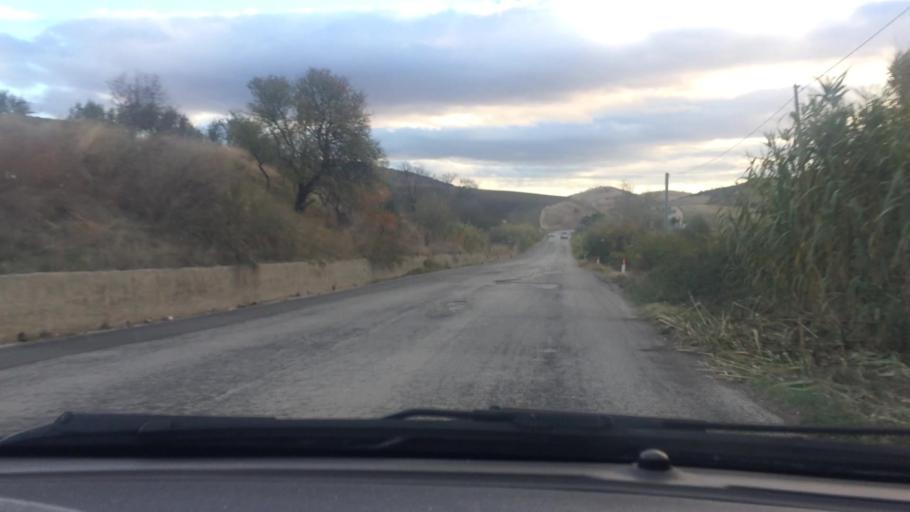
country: IT
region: Basilicate
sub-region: Provincia di Potenza
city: Tolve
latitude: 40.7145
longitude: 16.0237
